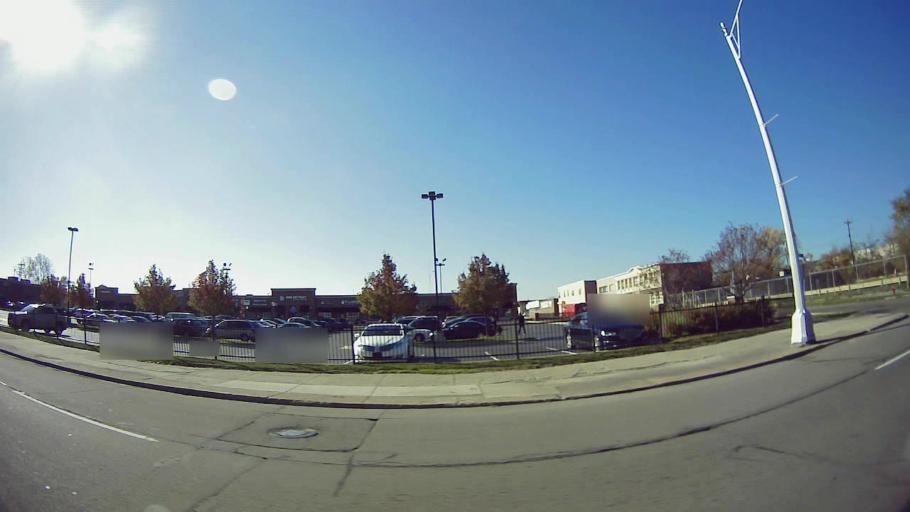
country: US
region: Michigan
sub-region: Wayne County
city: Highland Park
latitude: 42.4107
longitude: -83.1006
